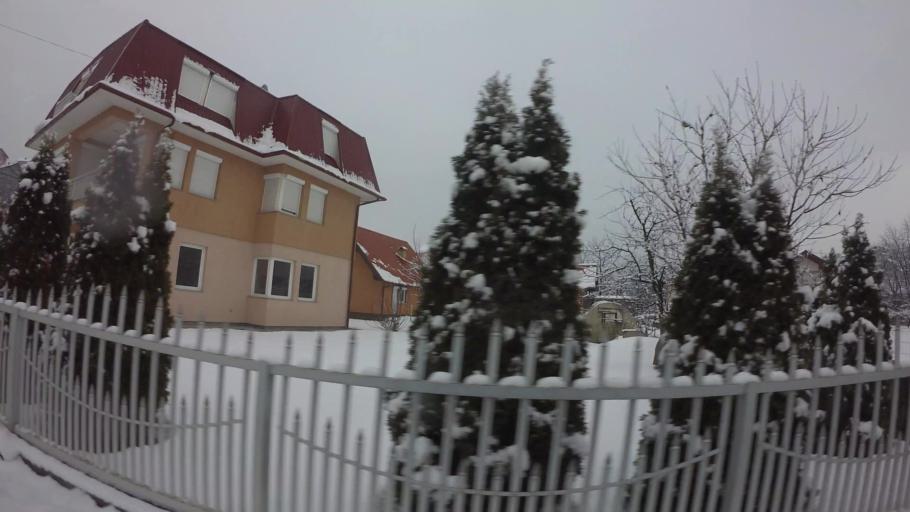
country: BA
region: Federation of Bosnia and Herzegovina
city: Vogosca
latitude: 43.8773
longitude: 18.3155
